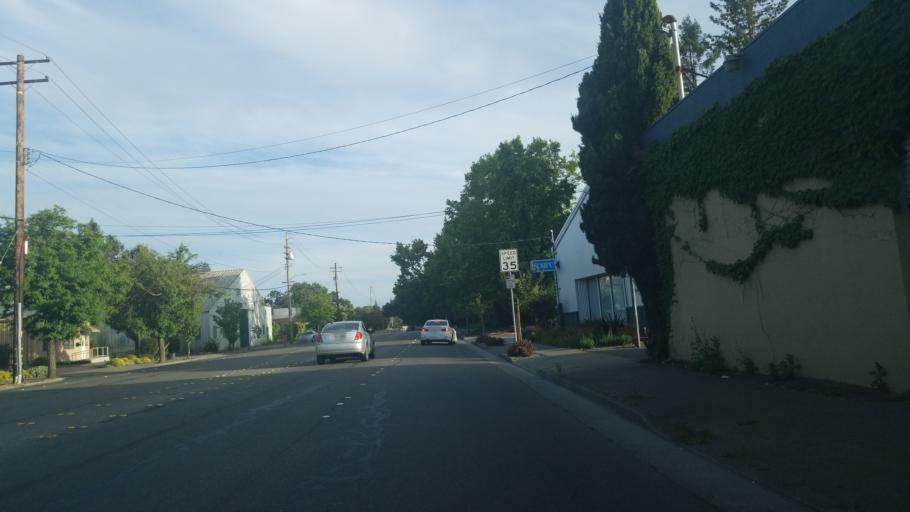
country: US
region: California
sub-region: Sonoma County
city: Santa Rosa
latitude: 38.4455
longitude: -122.7306
